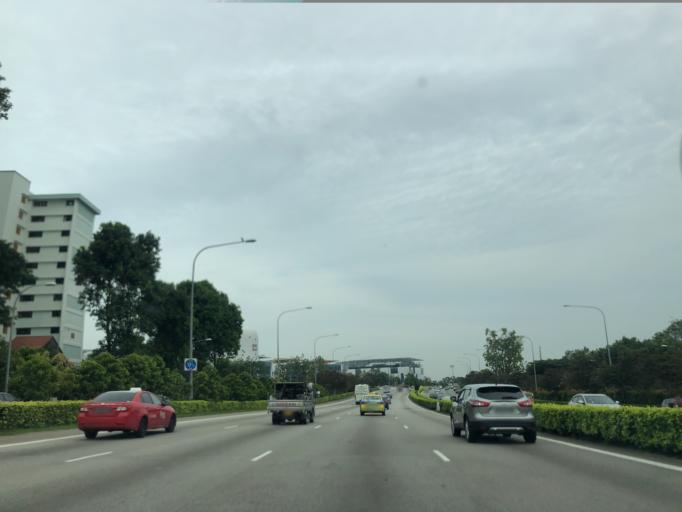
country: SG
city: Singapore
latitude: 1.3734
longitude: 103.8595
